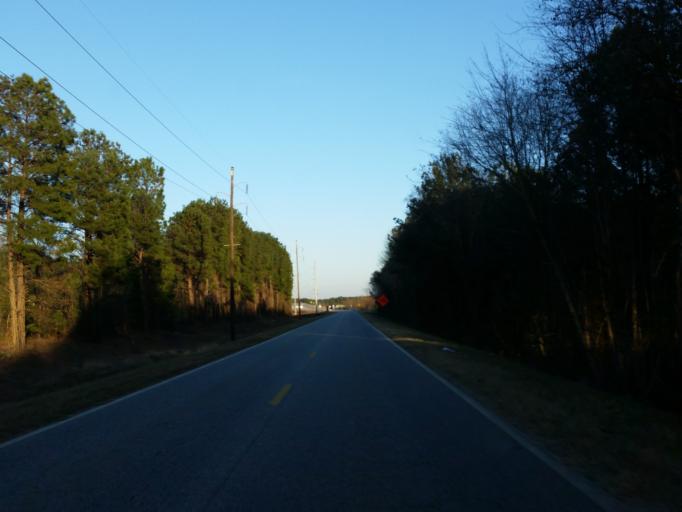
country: US
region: Georgia
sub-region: Crisp County
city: Cordele
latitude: 32.0040
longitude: -83.7673
